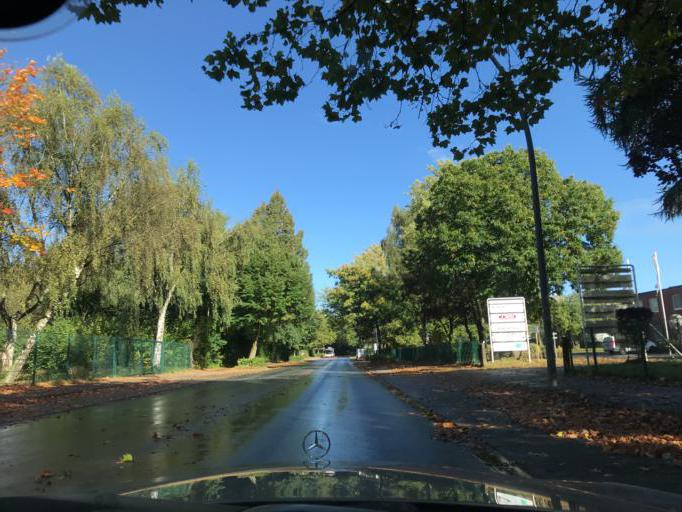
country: DE
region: Hamburg
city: Farmsen-Berne
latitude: 53.6218
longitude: 10.1549
